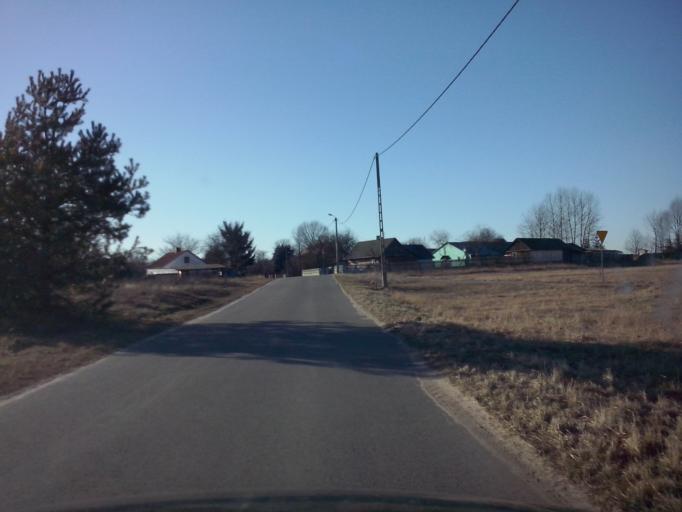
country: PL
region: Subcarpathian Voivodeship
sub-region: Powiat nizanski
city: Harasiuki
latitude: 50.5350
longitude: 22.4705
